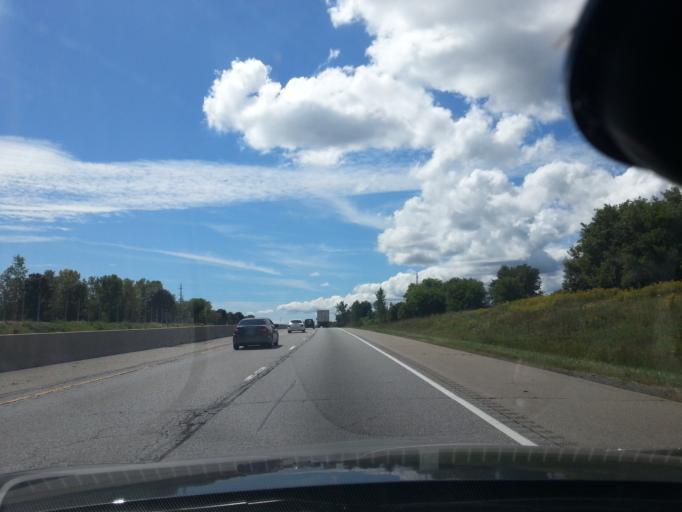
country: CA
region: Ontario
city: Brockville
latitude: 44.6176
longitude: -75.6766
